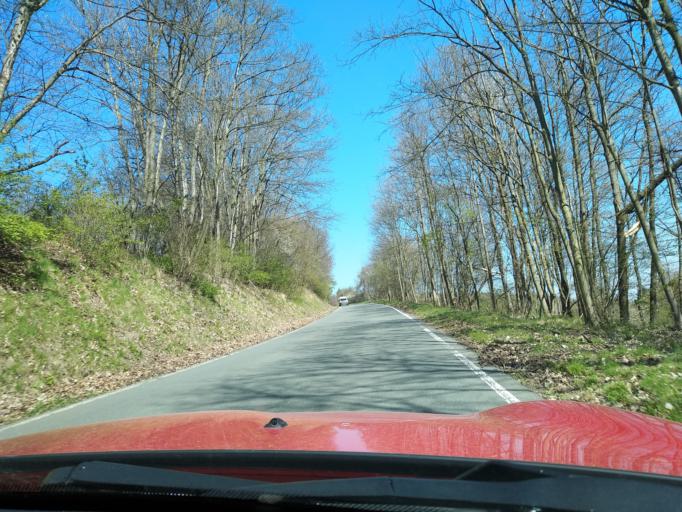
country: DE
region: Thuringia
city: Bad Blankenburg
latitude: 50.6506
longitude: 11.2824
